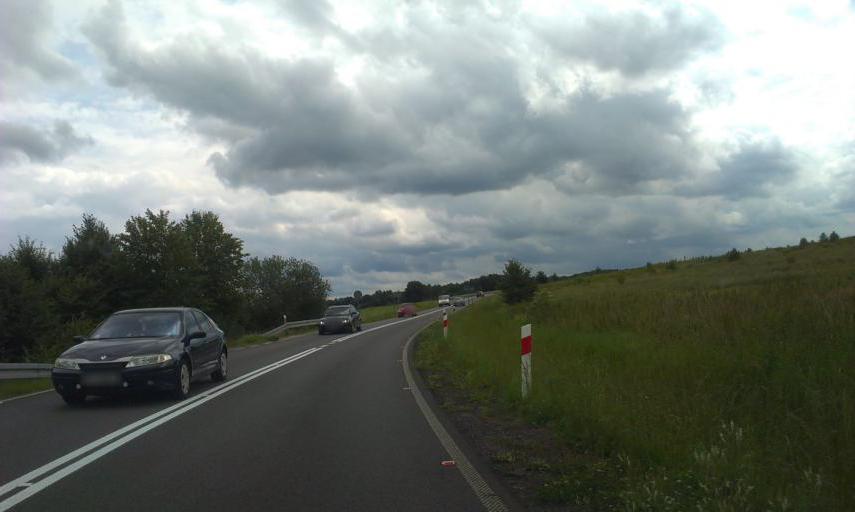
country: PL
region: West Pomeranian Voivodeship
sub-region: Koszalin
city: Koszalin
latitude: 54.1169
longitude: 16.1686
